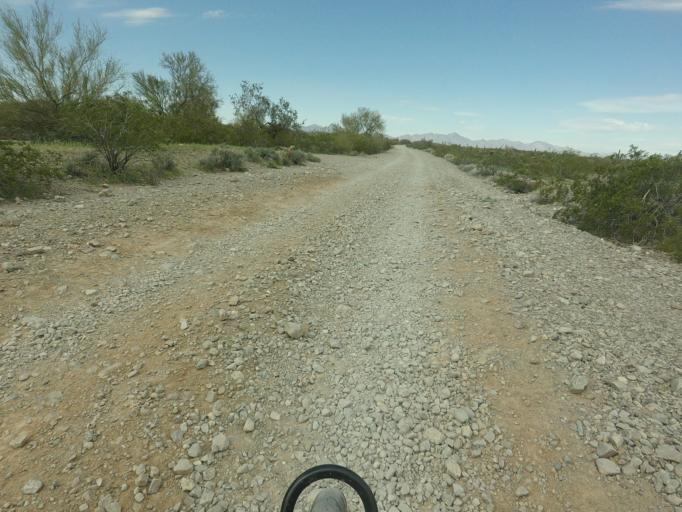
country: US
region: Arizona
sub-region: La Paz County
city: Quartzsite
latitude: 33.5230
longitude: -114.1211
